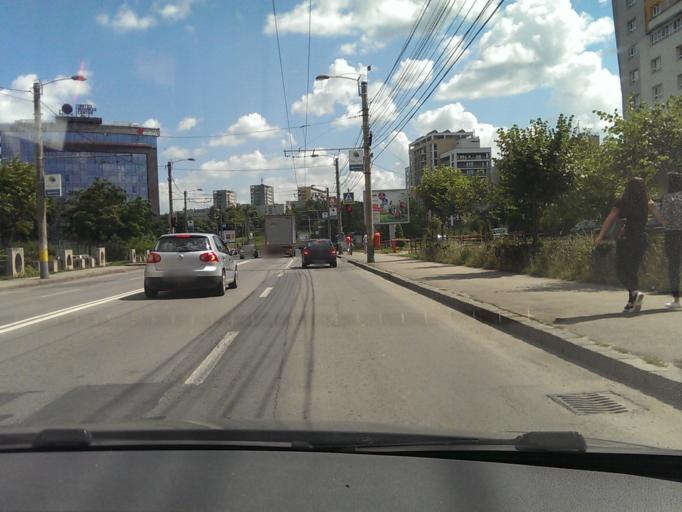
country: RO
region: Cluj
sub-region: Municipiul Cluj-Napoca
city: Cluj-Napoca
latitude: 46.7749
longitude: 23.6213
